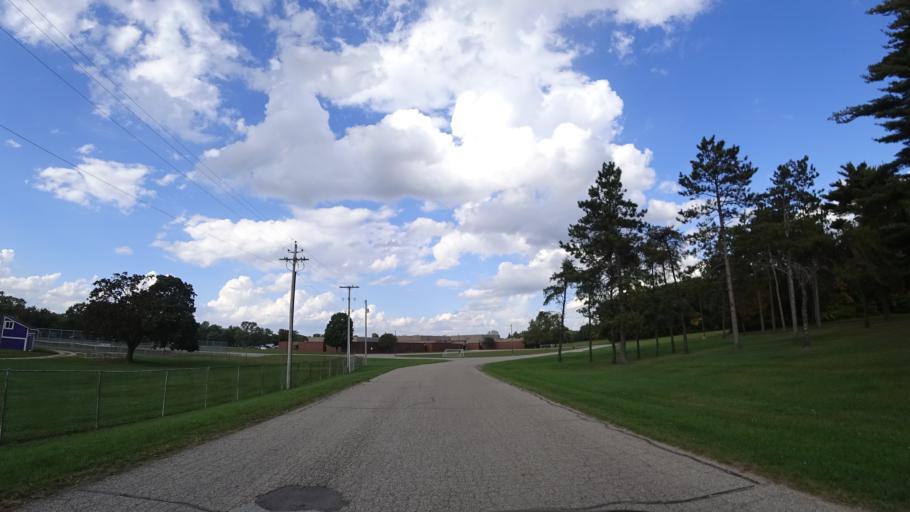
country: US
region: Michigan
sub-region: Saint Joseph County
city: Three Rivers
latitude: 41.9506
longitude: -85.6174
